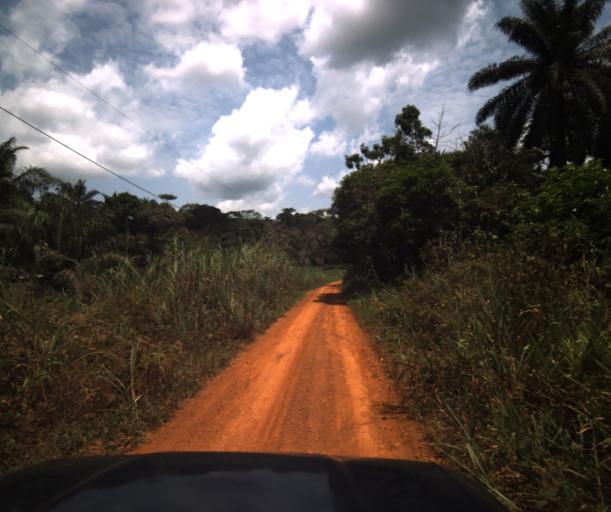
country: CM
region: Centre
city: Eseka
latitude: 3.5483
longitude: 10.9268
